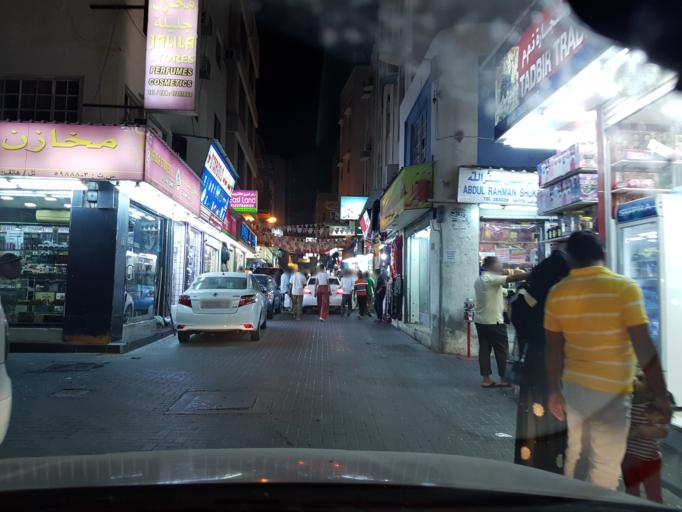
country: BH
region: Manama
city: Manama
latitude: 26.2322
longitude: 50.5751
